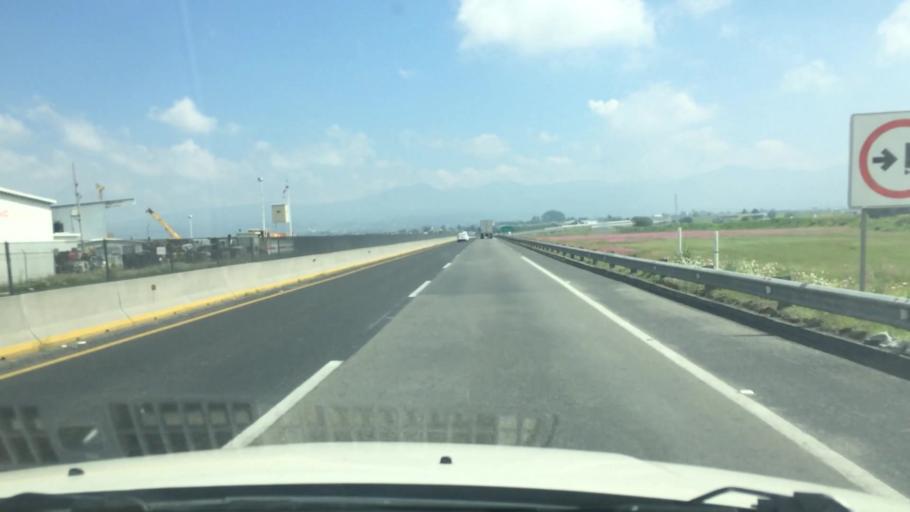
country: MX
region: Mexico
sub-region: Temoaya
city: Llano de la Y
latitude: 19.4057
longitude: -99.6279
